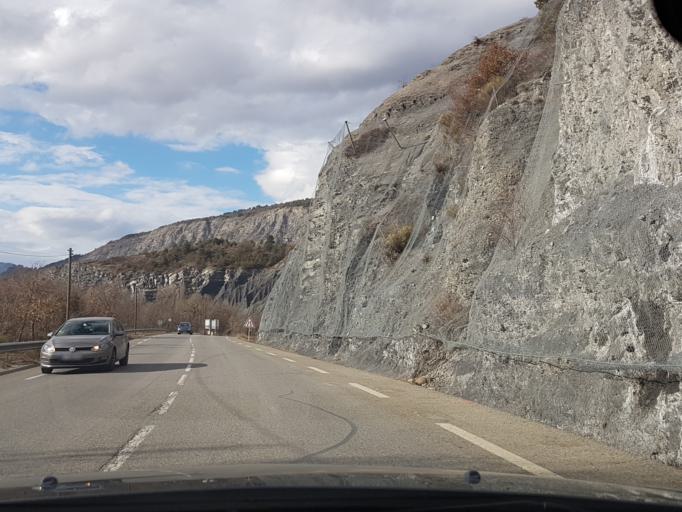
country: FR
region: Provence-Alpes-Cote d'Azur
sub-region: Departement des Hautes-Alpes
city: Tallard
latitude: 44.4794
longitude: 6.0860
